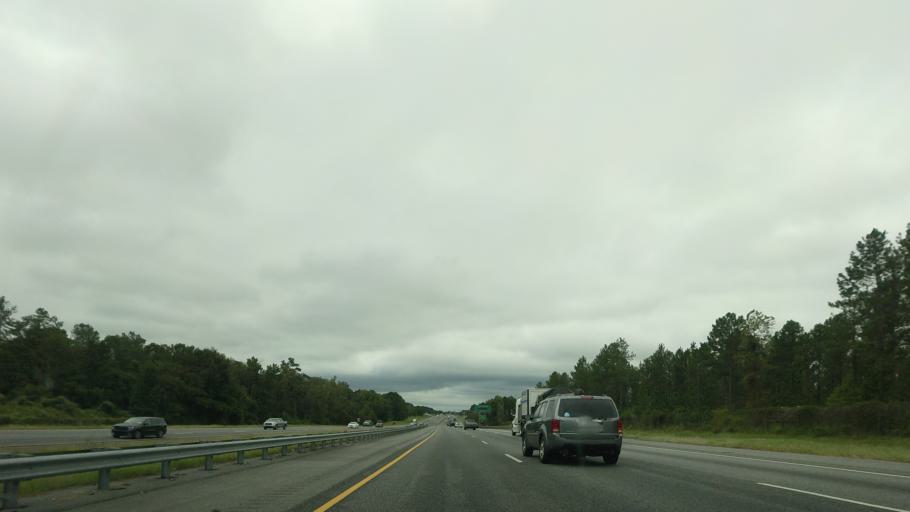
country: US
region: Georgia
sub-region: Lowndes County
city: Hahira
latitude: 30.9287
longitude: -83.3686
